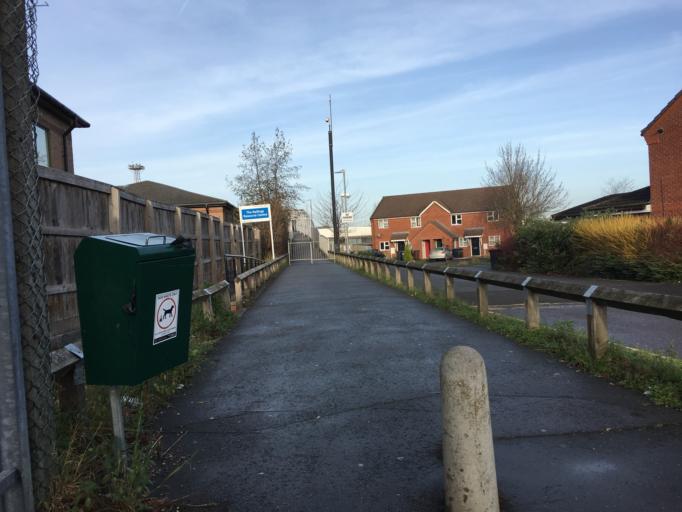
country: GB
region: England
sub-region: Warwickshire
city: Rugby
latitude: 52.3791
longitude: -1.2587
